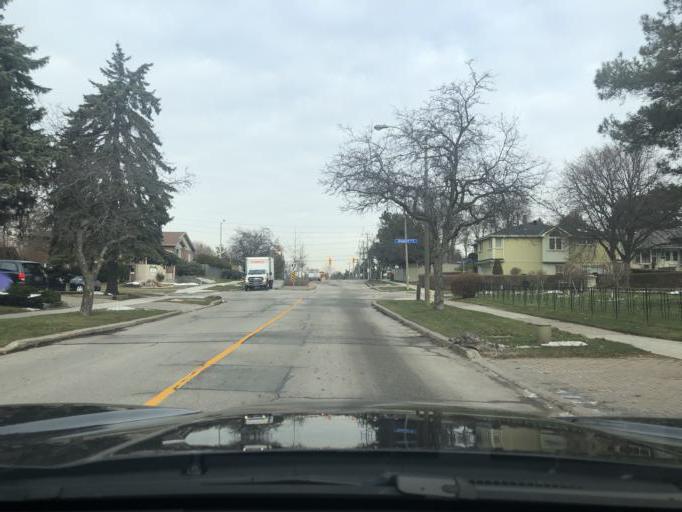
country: CA
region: Ontario
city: Willowdale
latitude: 43.7727
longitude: -79.3529
